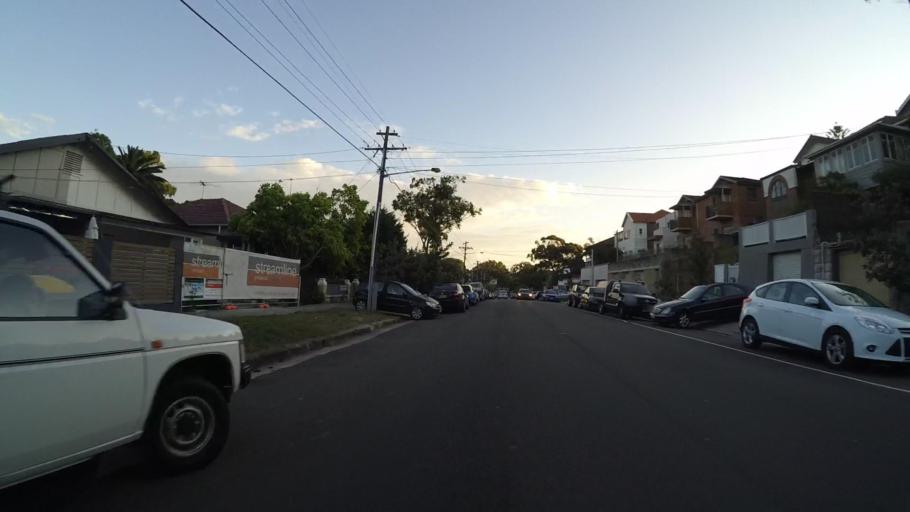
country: AU
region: New South Wales
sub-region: Randwick
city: Coogee
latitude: -33.9246
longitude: 151.2511
